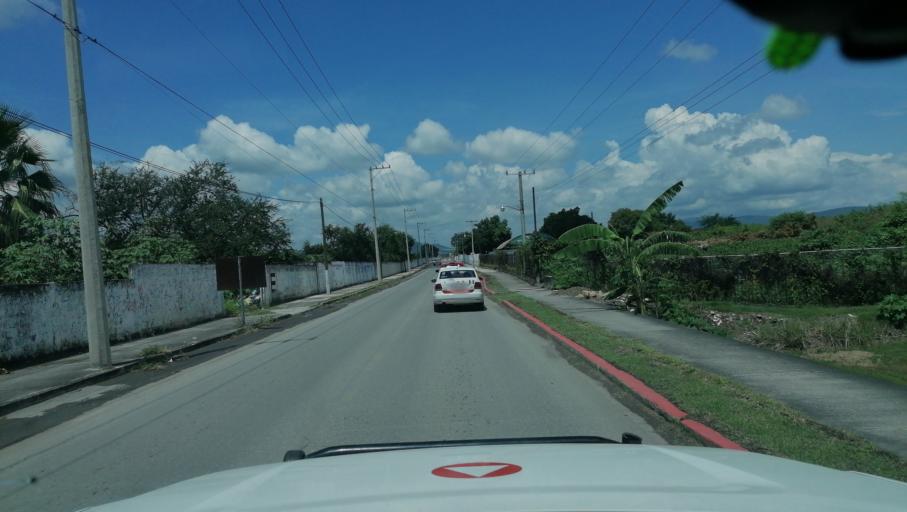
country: MX
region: Morelos
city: Zacatepec
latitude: 18.6488
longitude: -99.1841
